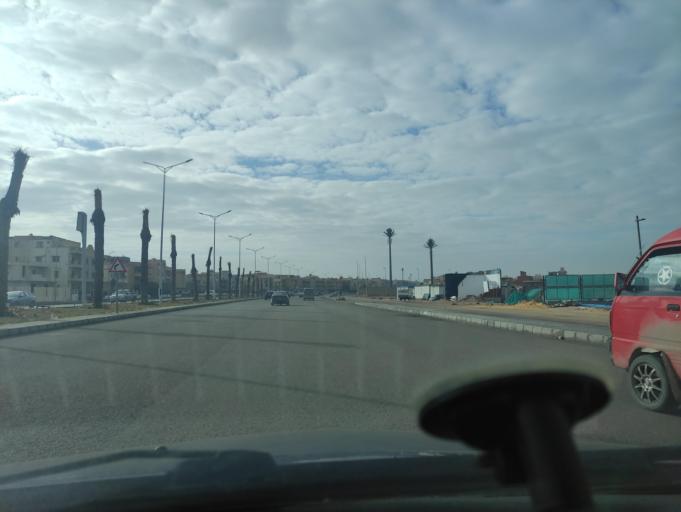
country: EG
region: Muhafazat al Qalyubiyah
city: Al Khankah
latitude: 30.0493
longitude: 31.4422
